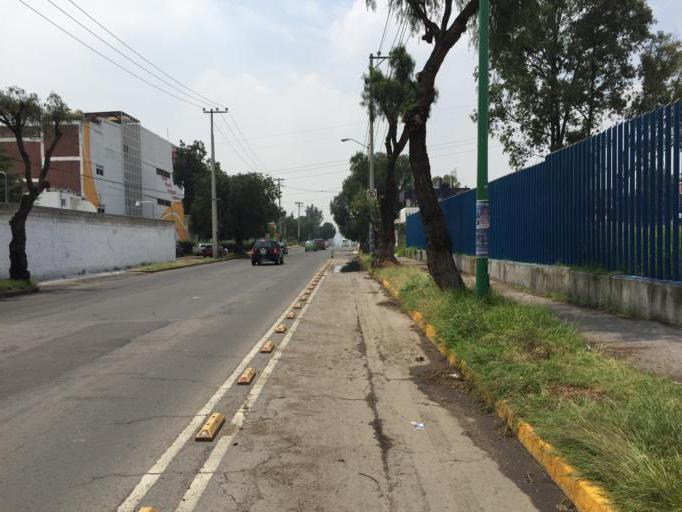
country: MX
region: Mexico
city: Cuautitlan Izcalli
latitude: 19.6400
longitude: -99.2034
